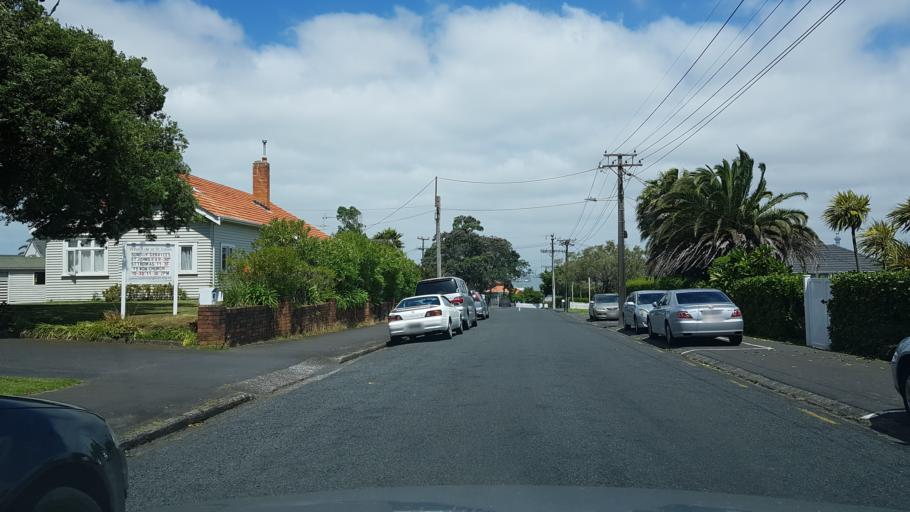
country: NZ
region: Auckland
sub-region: Auckland
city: North Shore
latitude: -36.8116
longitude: 174.7421
